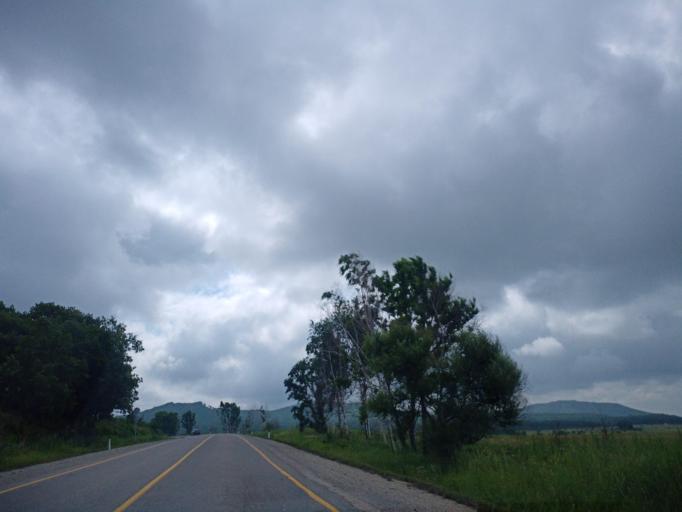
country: RU
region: Primorskiy
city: Dal'nerechensk
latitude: 46.0382
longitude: 133.8843
